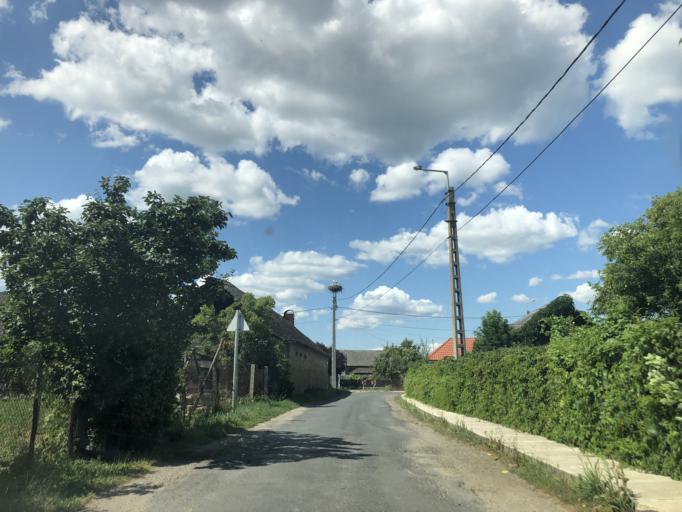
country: HU
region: Borsod-Abauj-Zemplen
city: Szendro
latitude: 48.5458
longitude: 20.7622
